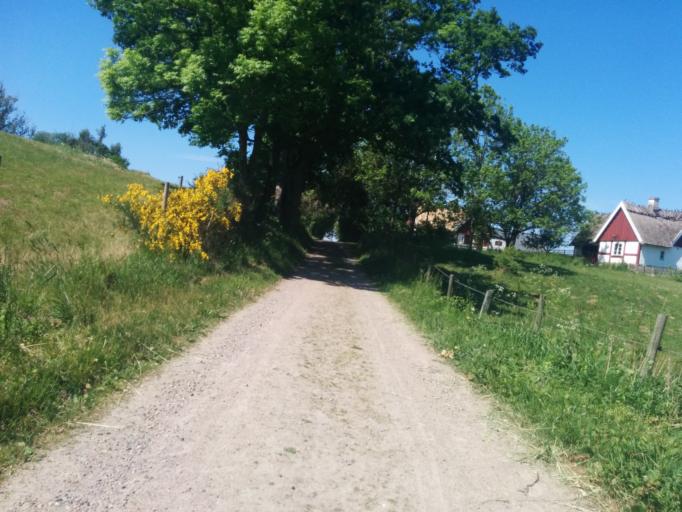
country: SE
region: Skane
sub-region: Lunds Kommun
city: Genarp
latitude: 55.5875
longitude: 13.3836
